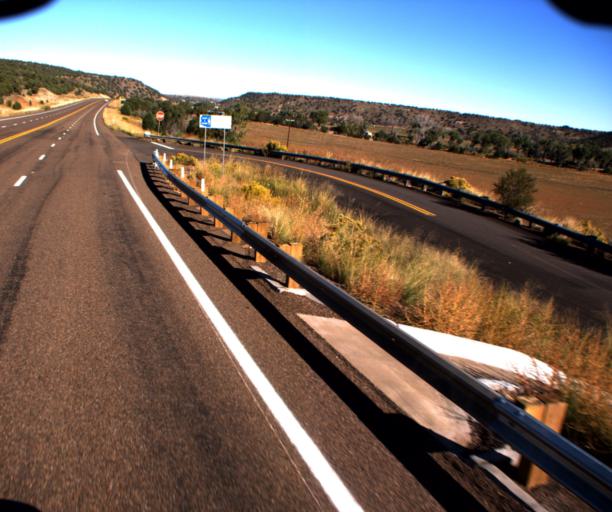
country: US
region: Arizona
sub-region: Navajo County
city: White Mountain Lake
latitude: 34.3778
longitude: -110.0554
